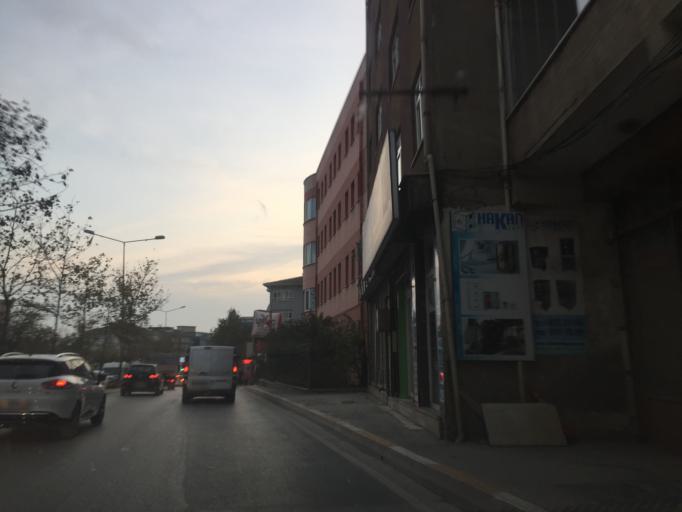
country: TR
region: Istanbul
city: Samandira
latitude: 40.9834
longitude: 29.2217
